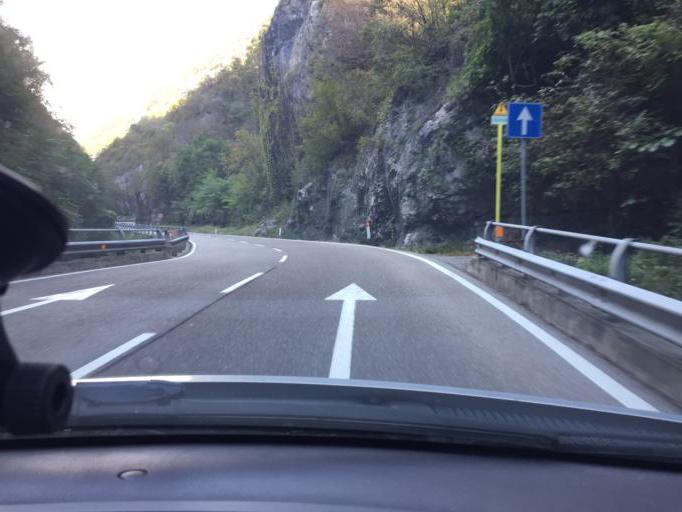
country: IT
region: Trentino-Alto Adige
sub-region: Provincia di Trento
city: Cadine
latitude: 46.0807
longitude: 11.0874
